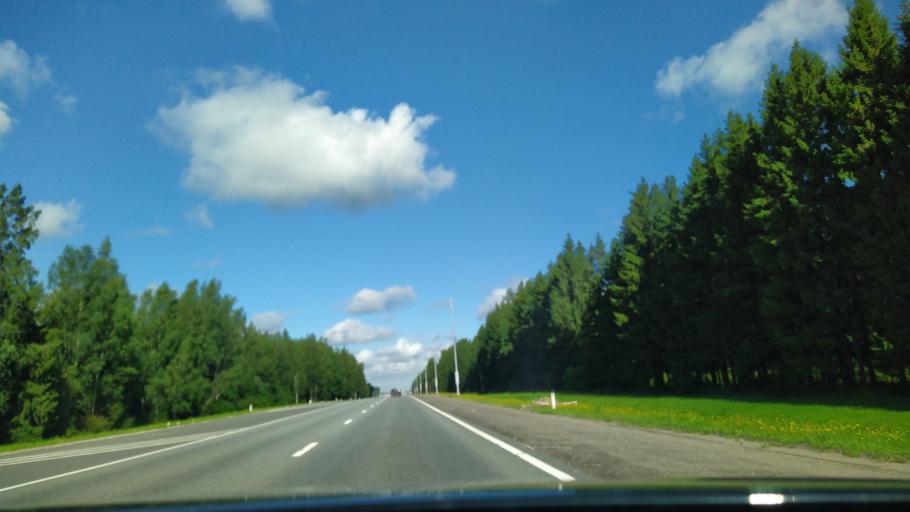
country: RU
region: Leningrad
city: Ul'yanovka
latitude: 59.5924
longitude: 30.7836
